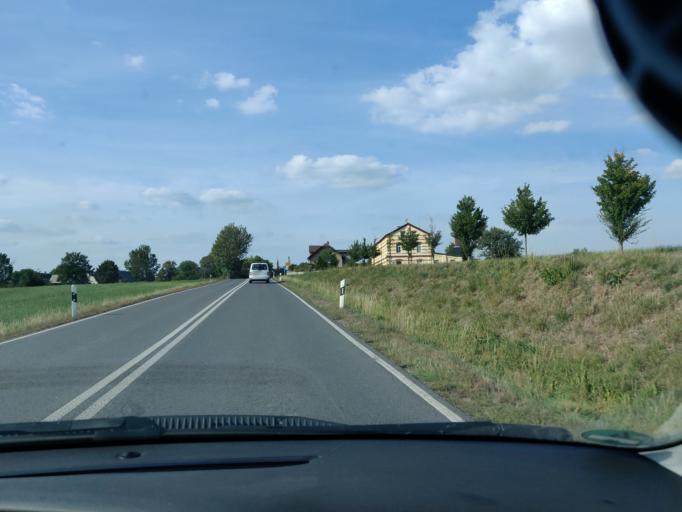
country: DE
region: Saxony
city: Erlau
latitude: 51.0059
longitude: 12.9484
